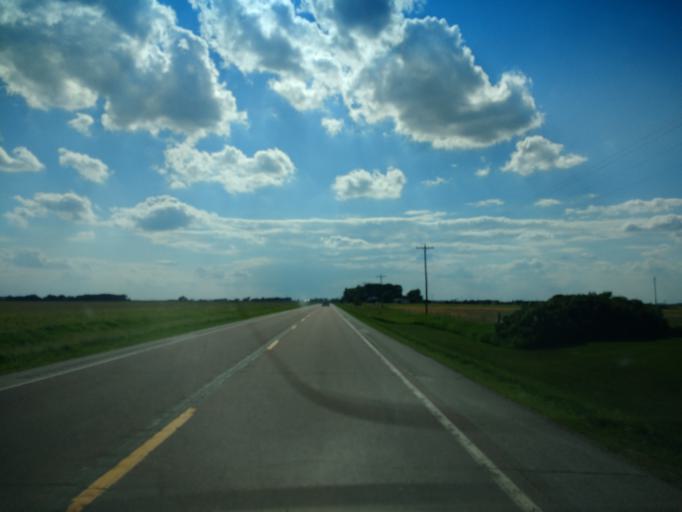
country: US
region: Iowa
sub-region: Clay County
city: Spencer
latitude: 43.1839
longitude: -95.2102
